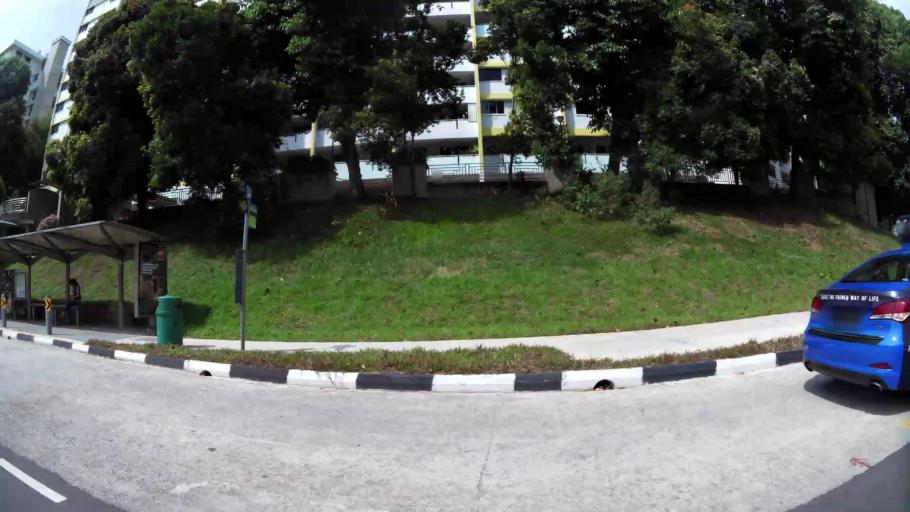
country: SG
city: Singapore
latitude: 1.3181
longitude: 103.7713
